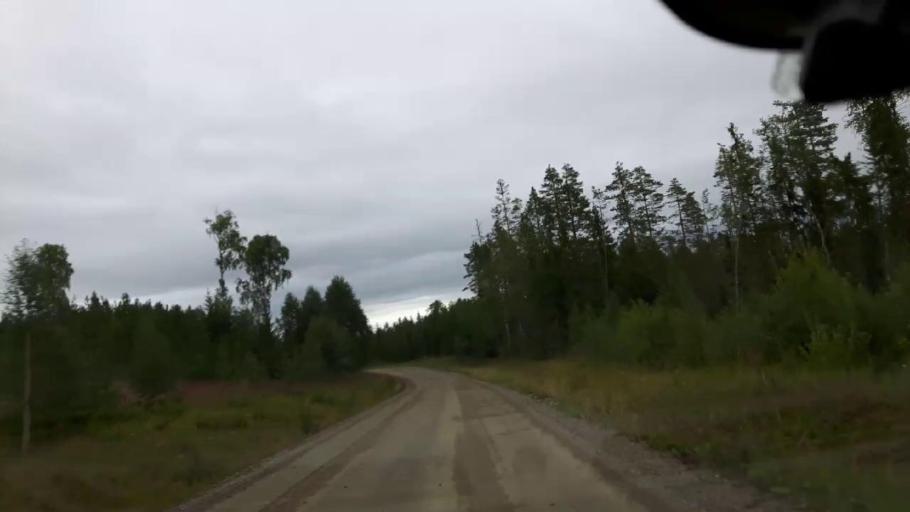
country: SE
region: Vaesternorrland
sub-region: Ange Kommun
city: Fransta
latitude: 62.7765
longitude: 15.9619
